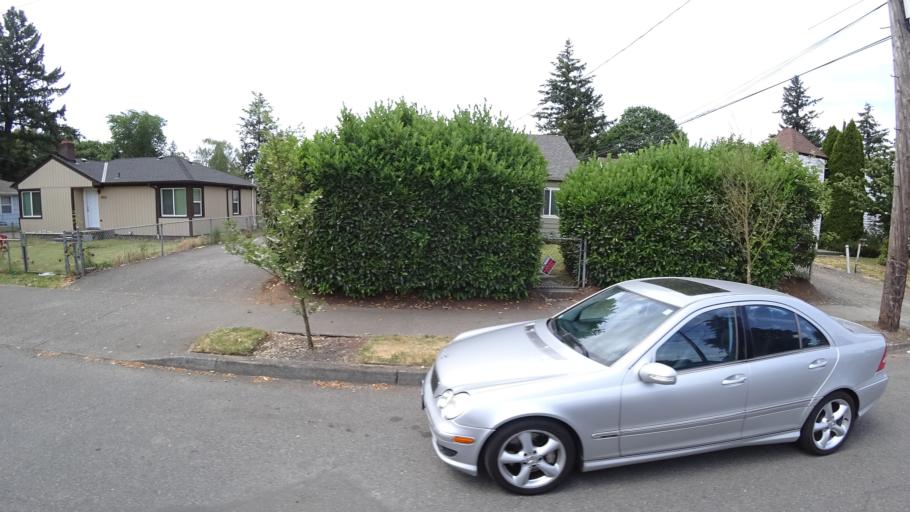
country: US
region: Oregon
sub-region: Multnomah County
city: Lents
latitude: 45.4669
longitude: -122.5894
